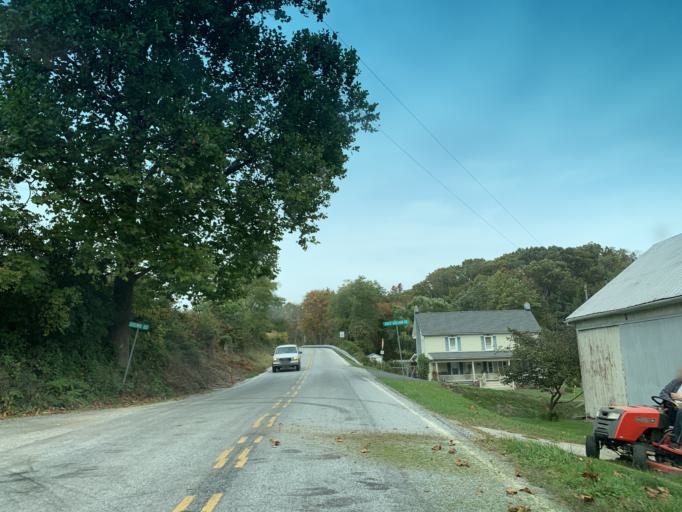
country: US
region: Pennsylvania
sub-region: York County
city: Windsor
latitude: 39.8441
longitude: -76.5090
